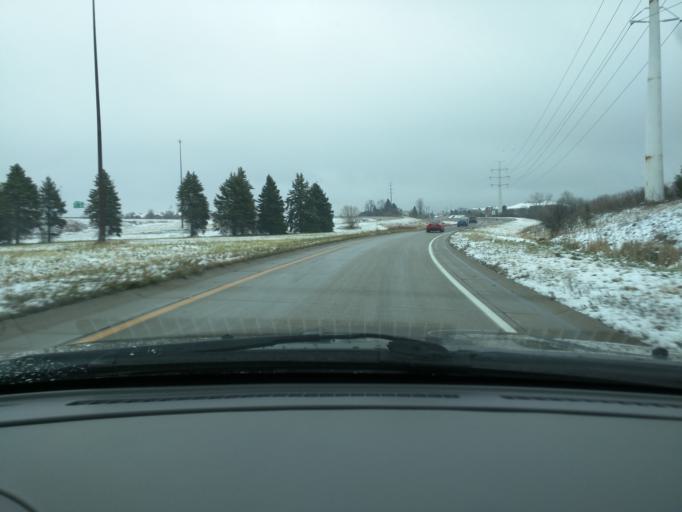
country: US
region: Minnesota
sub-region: Hennepin County
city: Eden Prairie
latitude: 44.8637
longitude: -93.4331
